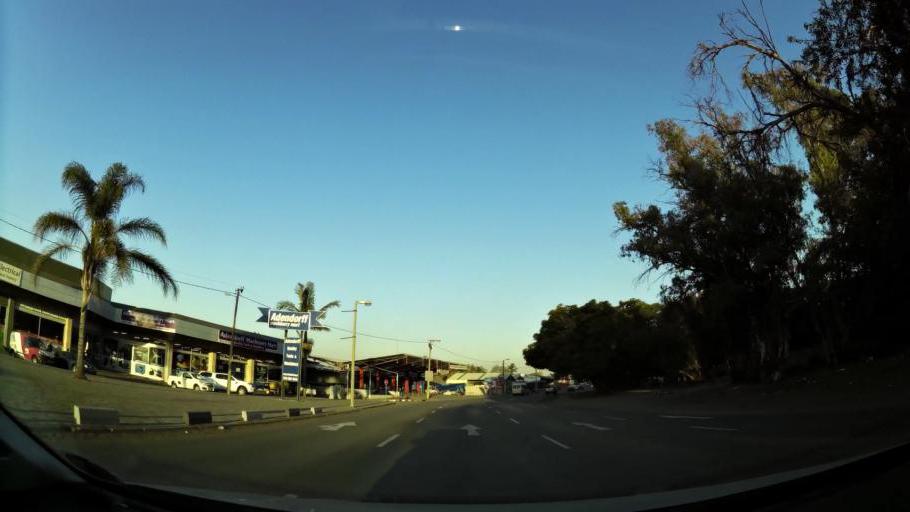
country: ZA
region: North-West
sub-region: Bojanala Platinum District Municipality
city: Rustenburg
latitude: -25.6712
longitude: 27.2476
